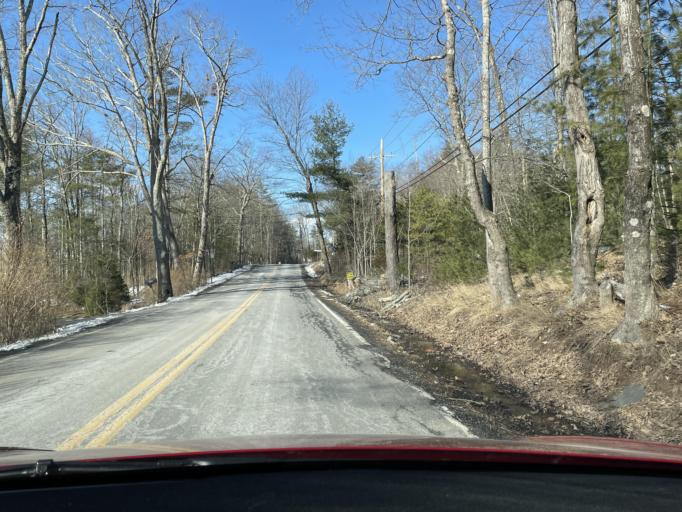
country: US
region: New York
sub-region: Ulster County
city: Woodstock
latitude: 42.0494
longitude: -74.1271
